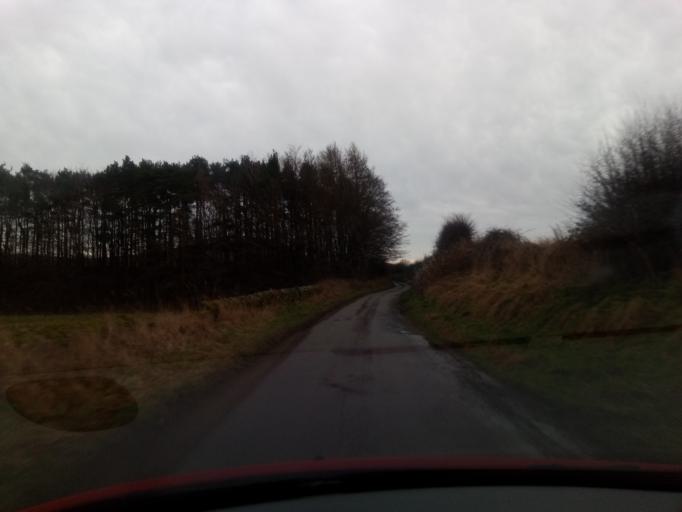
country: GB
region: England
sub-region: Northumberland
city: Whittingham
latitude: 55.4949
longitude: -1.9087
